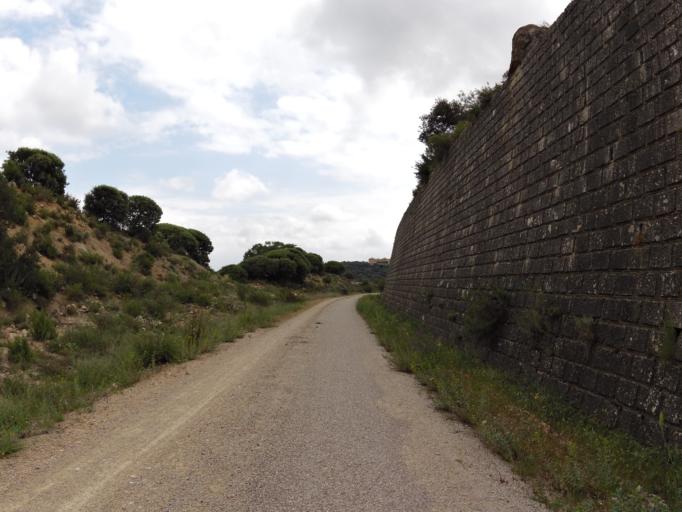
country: ES
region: Castille-La Mancha
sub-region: Provincia de Albacete
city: Robledo
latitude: 38.7740
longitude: -2.3981
